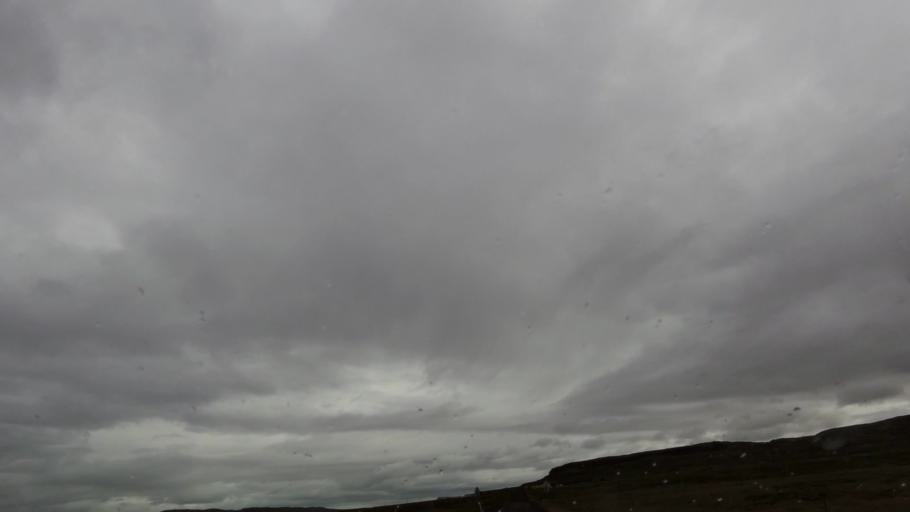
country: IS
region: West
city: Borgarnes
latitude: 65.0246
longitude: -22.1078
